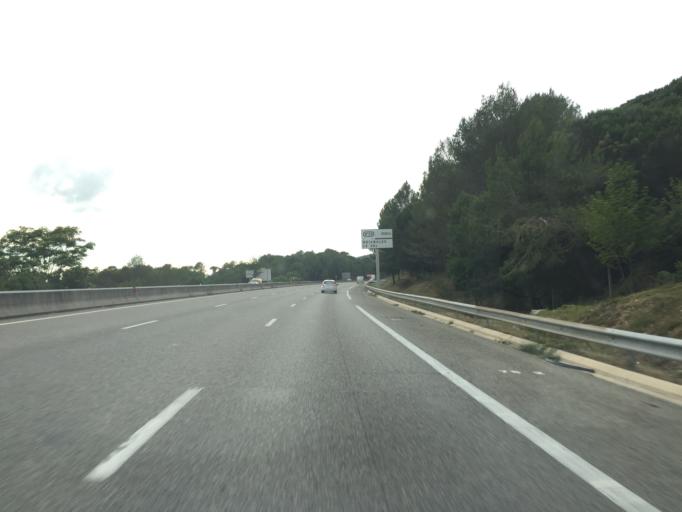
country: FR
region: Provence-Alpes-Cote d'Azur
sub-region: Departement du Var
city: Le Val
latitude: 43.4191
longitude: 6.0841
